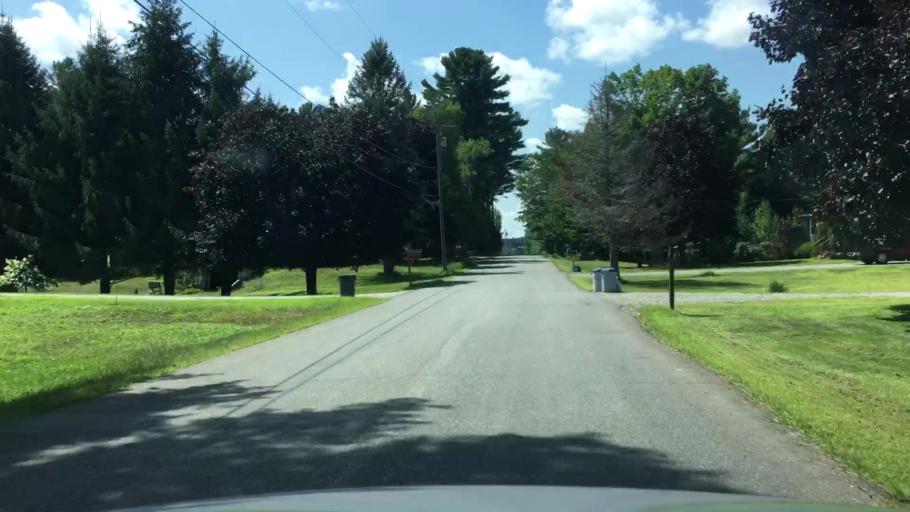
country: US
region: Maine
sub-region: Kennebec County
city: Manchester
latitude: 44.3538
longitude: -69.8280
